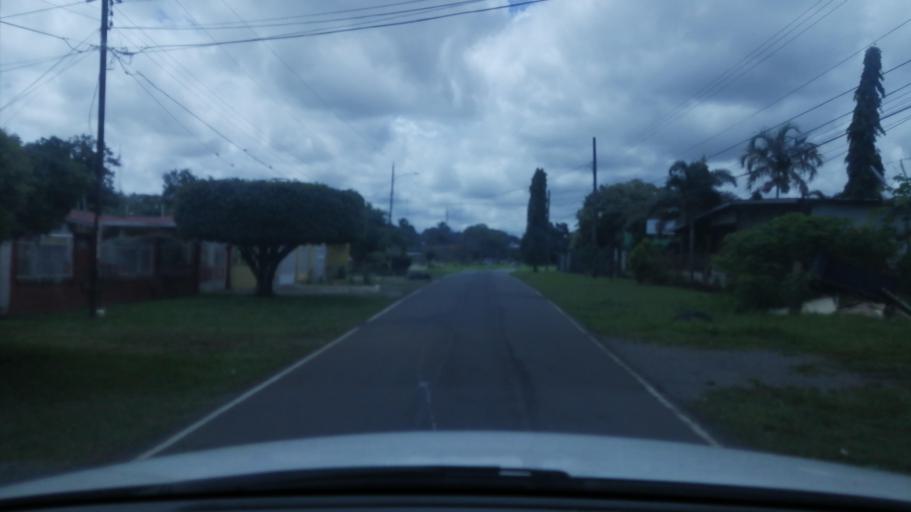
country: PA
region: Chiriqui
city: David
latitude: 8.4164
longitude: -82.4287
